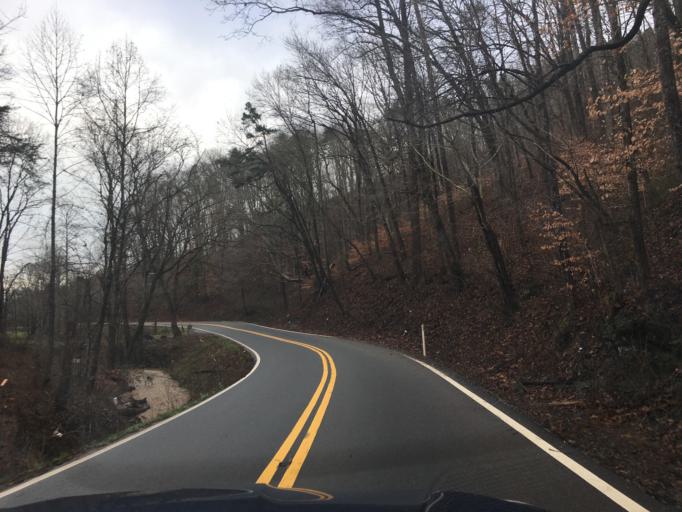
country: US
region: Tennessee
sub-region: McMinn County
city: Englewood
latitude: 35.4017
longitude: -84.4465
